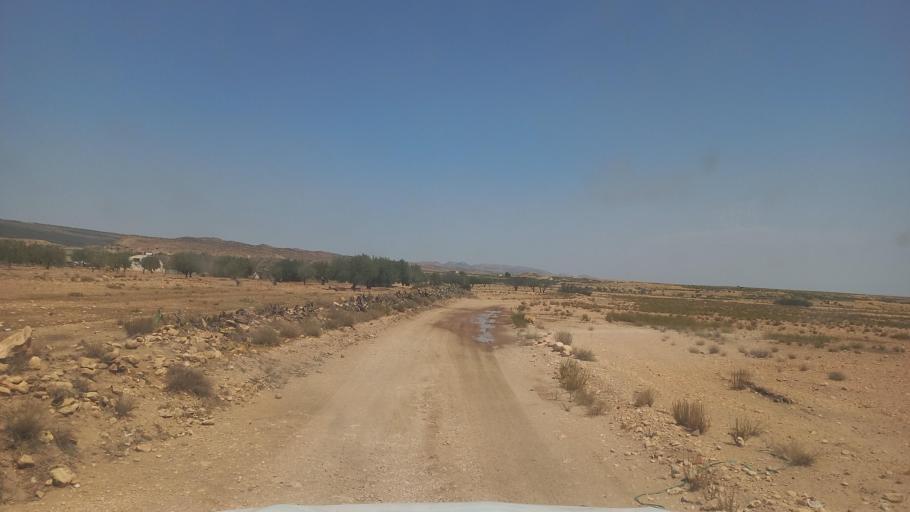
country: TN
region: Al Qasrayn
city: Kasserine
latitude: 35.2887
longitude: 8.9515
